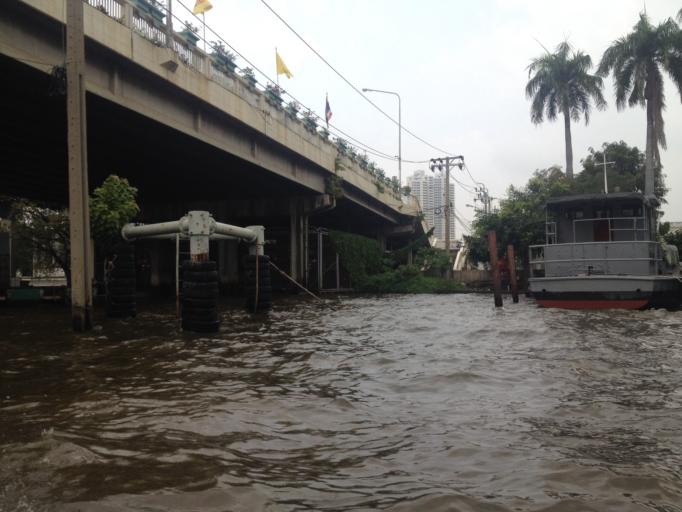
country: TH
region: Bangkok
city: Bangkok Noi
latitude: 13.7614
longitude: 100.4828
